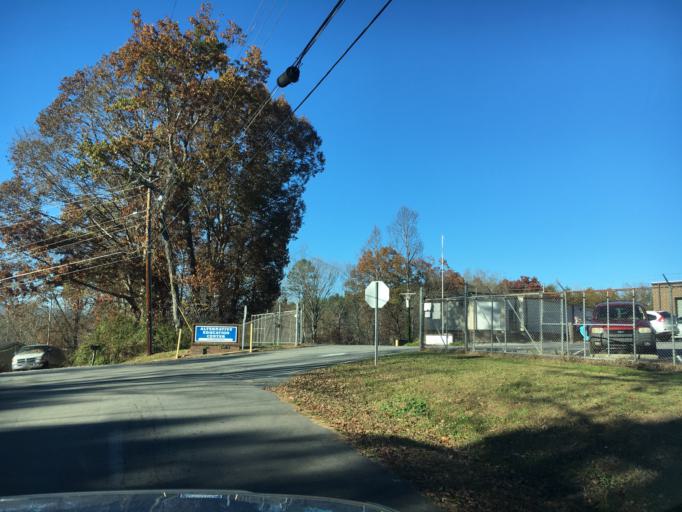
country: US
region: North Carolina
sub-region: McDowell County
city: West Marion
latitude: 35.6585
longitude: -82.0282
